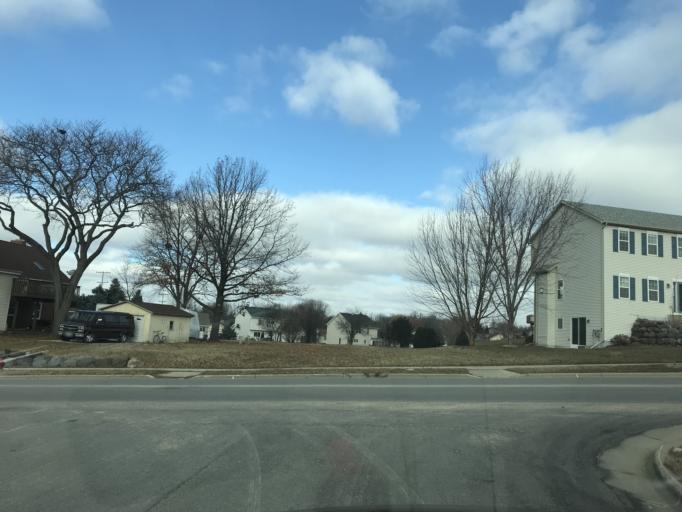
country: US
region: Wisconsin
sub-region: Dane County
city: Monona
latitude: 43.1148
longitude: -89.2951
